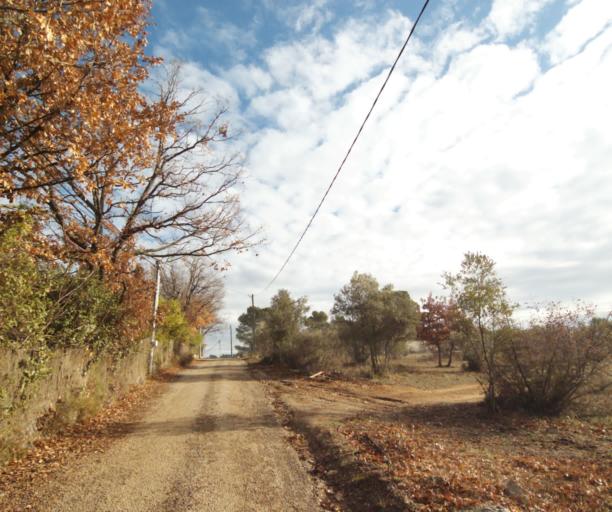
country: FR
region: Provence-Alpes-Cote d'Azur
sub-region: Departement du Var
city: Trans-en-Provence
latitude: 43.4925
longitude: 6.4721
